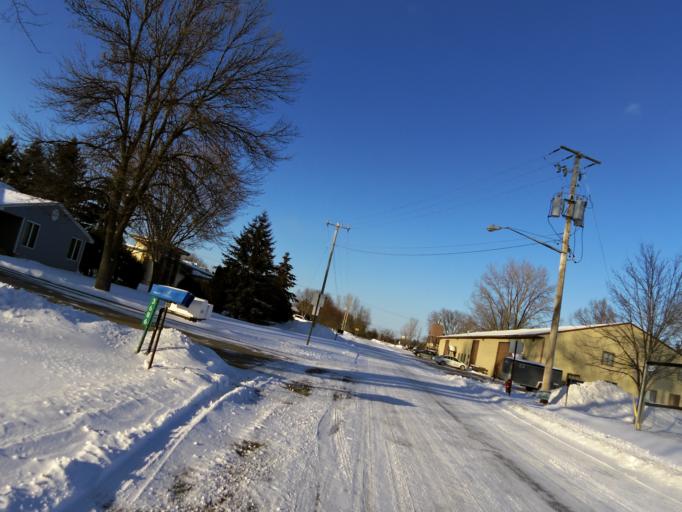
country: US
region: Minnesota
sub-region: Washington County
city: Lake Elmo
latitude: 45.0020
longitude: -92.8773
